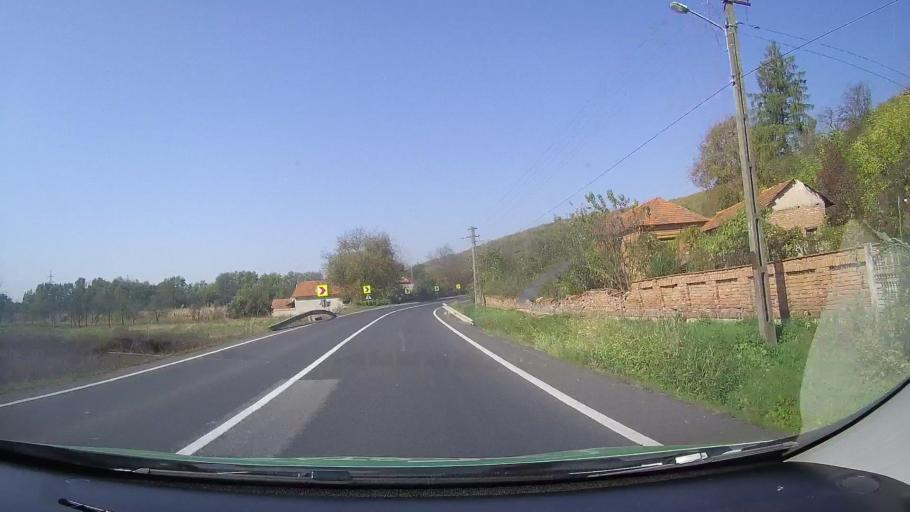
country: RO
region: Hunedoara
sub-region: Comuna Dobra
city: Dobra
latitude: 45.9386
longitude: 22.5421
